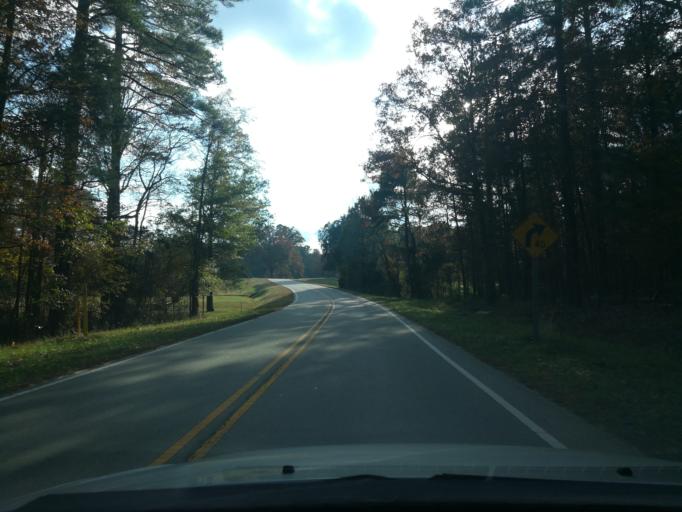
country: US
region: North Carolina
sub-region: Durham County
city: Durham
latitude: 36.0139
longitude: -78.9857
